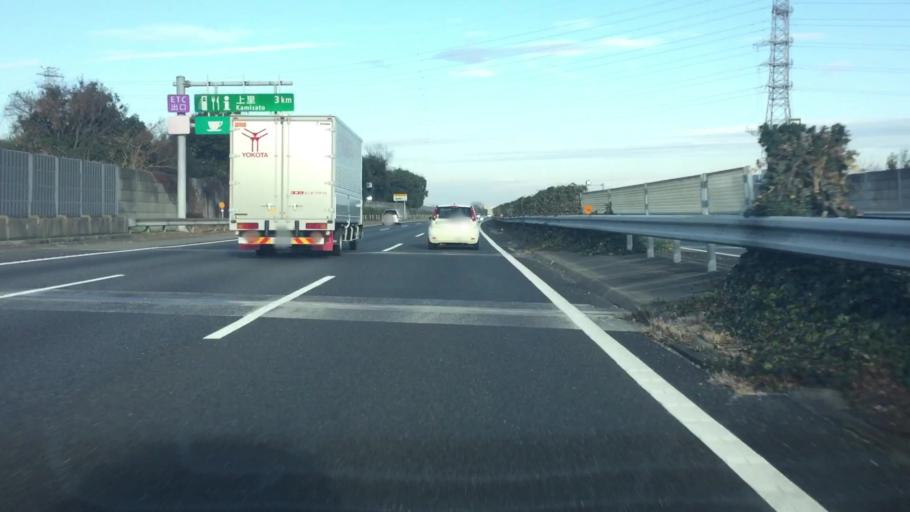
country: JP
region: Saitama
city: Honjo
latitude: 36.2358
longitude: 139.1477
